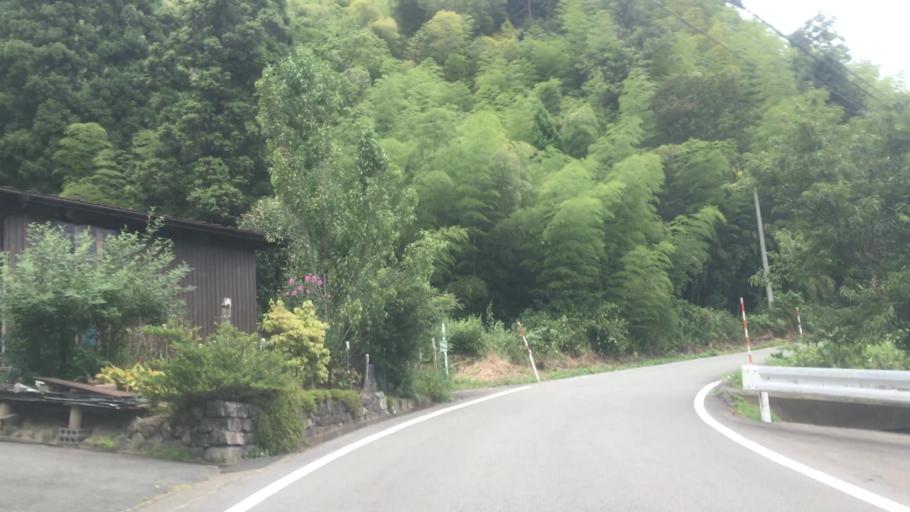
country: JP
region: Hyogo
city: Toyooka
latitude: 35.5977
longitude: 134.8008
